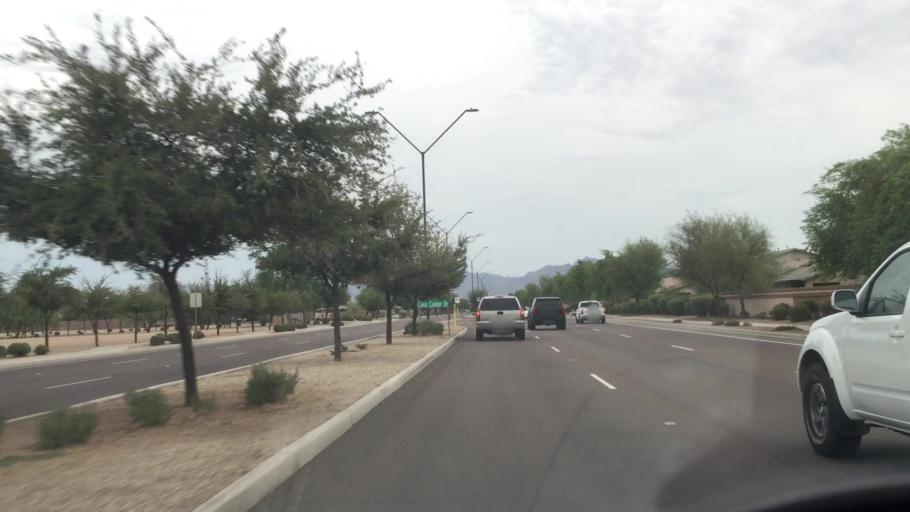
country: US
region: Arizona
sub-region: Maricopa County
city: Avondale
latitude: 33.4443
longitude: -112.3065
